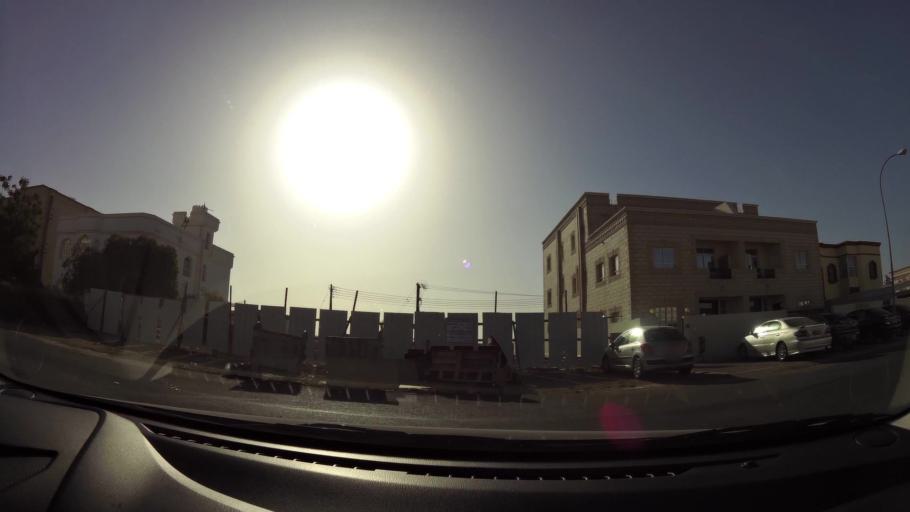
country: OM
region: Muhafazat Masqat
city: As Sib al Jadidah
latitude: 23.6004
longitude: 58.2062
